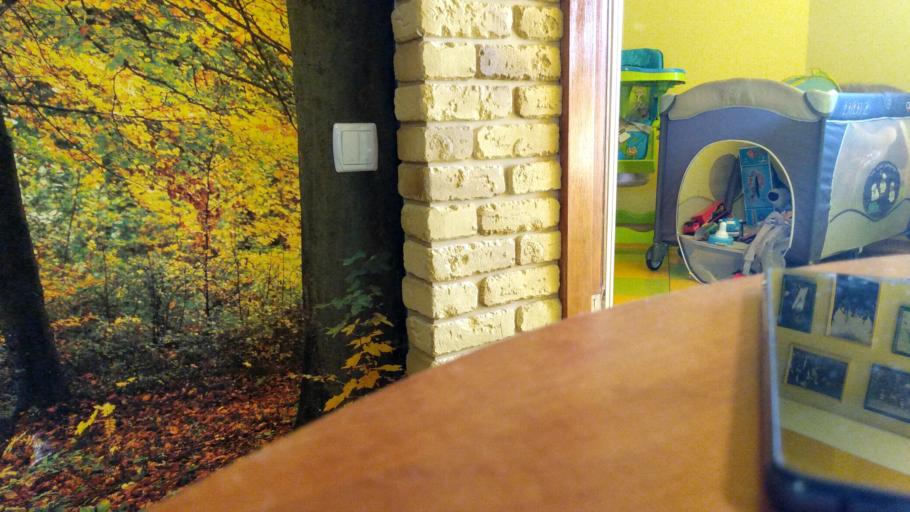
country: RU
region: Tverskaya
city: Kalashnikovo
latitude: 57.3580
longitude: 35.2336
